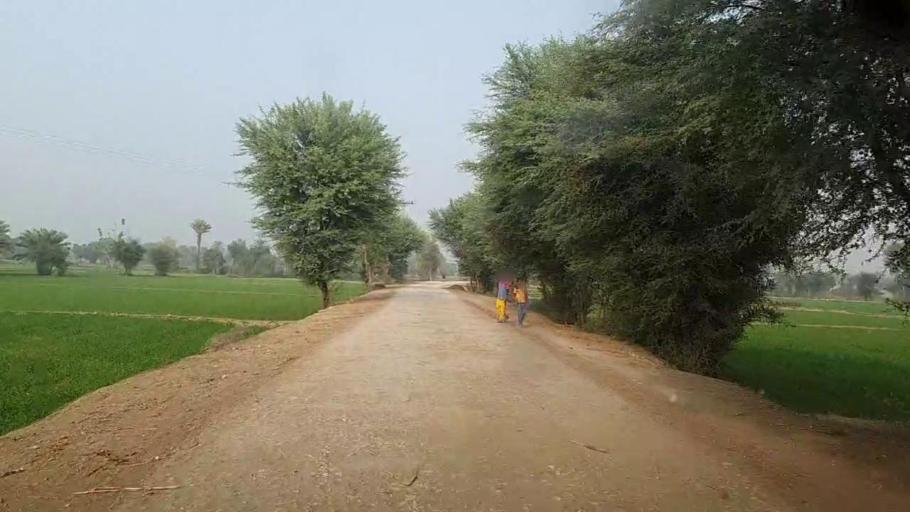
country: PK
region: Sindh
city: Bozdar
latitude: 27.1411
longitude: 68.6648
